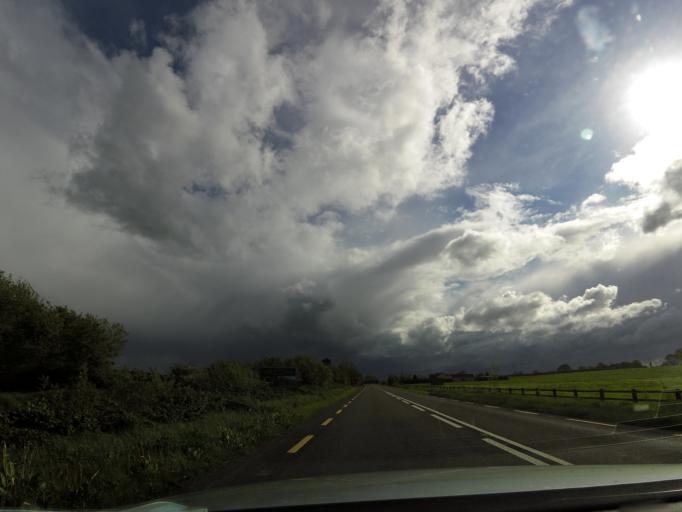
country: IE
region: Munster
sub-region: North Tipperary
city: Templemore
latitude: 52.7704
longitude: -7.8411
